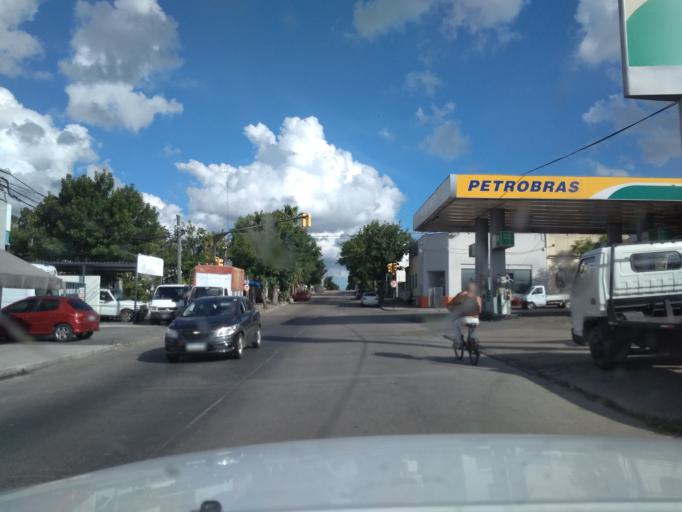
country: UY
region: Florida
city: Florida
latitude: -34.0936
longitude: -56.2136
